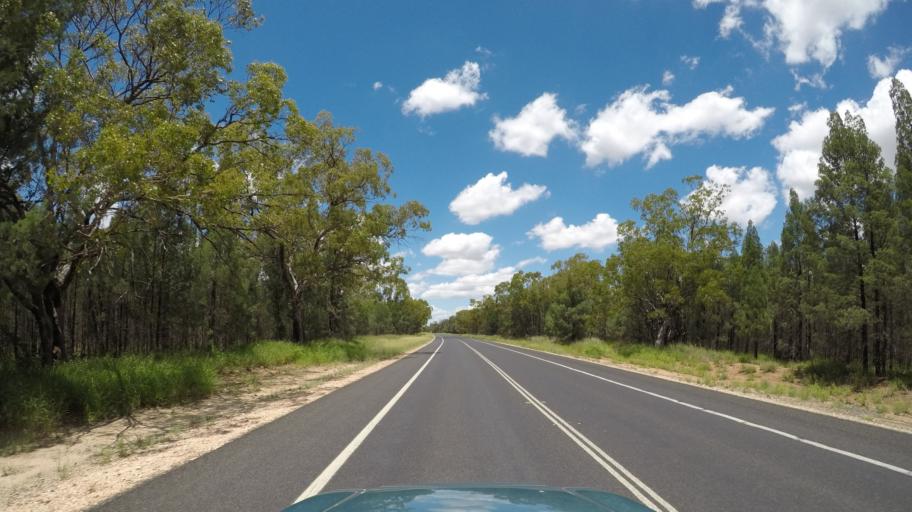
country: AU
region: Queensland
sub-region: Goondiwindi
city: Goondiwindi
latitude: -28.0921
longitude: 150.7288
